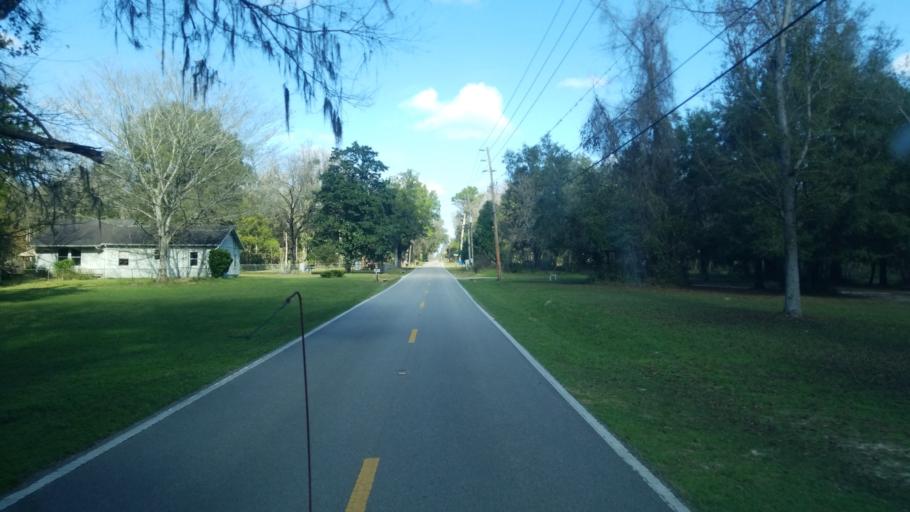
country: US
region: Florida
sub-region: Hernando County
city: North Brooksville
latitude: 28.6133
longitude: -82.3801
